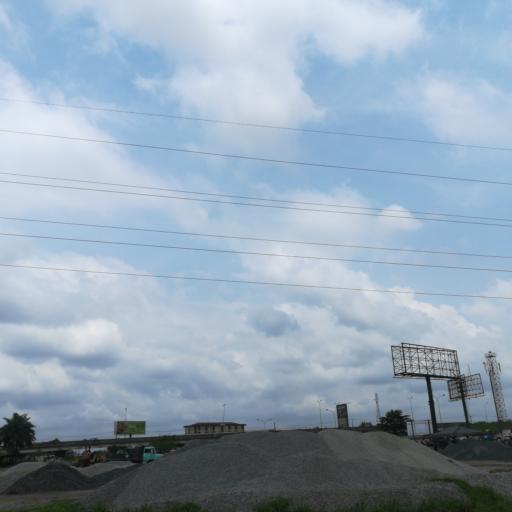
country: NG
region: Rivers
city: Port Harcourt
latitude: 4.8540
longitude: 7.0673
